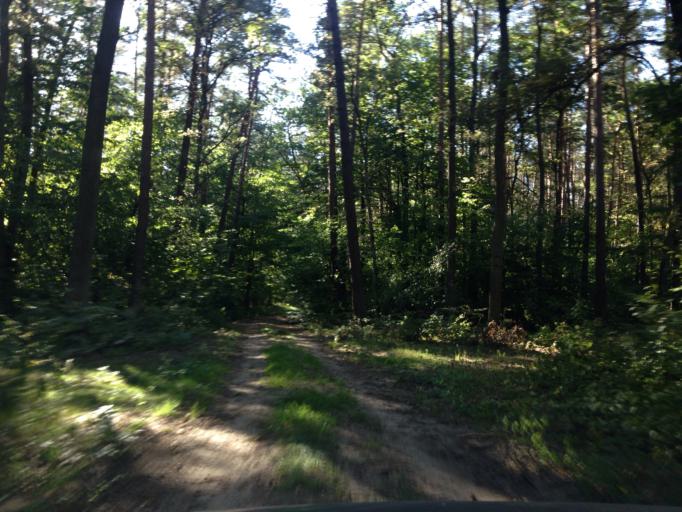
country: PL
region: Kujawsko-Pomorskie
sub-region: Powiat brodnicki
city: Gorzno
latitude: 53.1751
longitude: 19.6586
